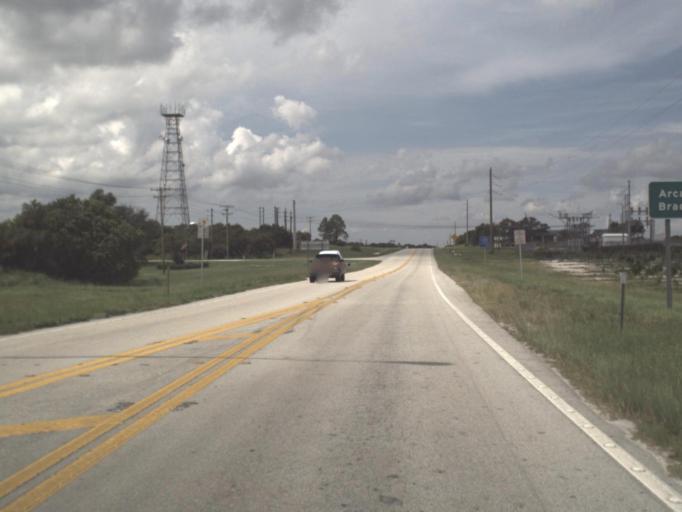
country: US
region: Florida
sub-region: Highlands County
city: Placid Lakes
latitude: 27.2085
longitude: -81.3306
